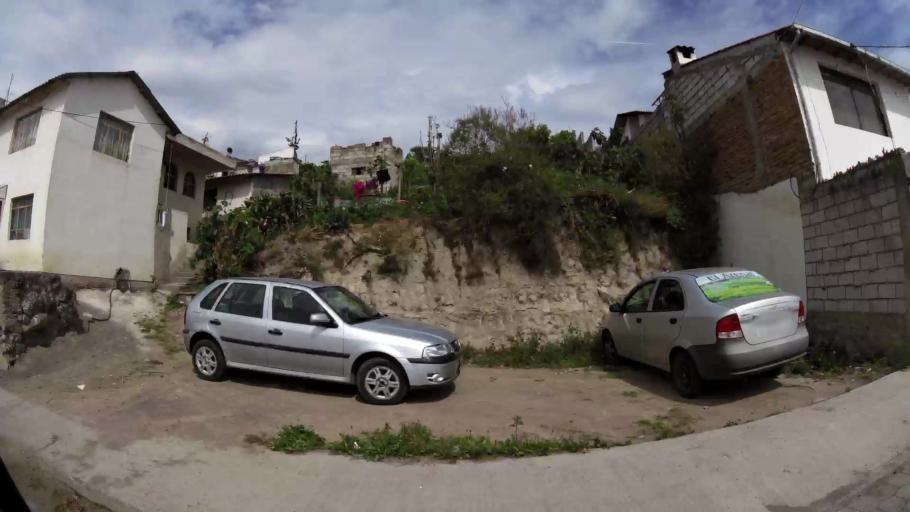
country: EC
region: Cotopaxi
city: Latacunga
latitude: -0.9265
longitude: -78.6037
